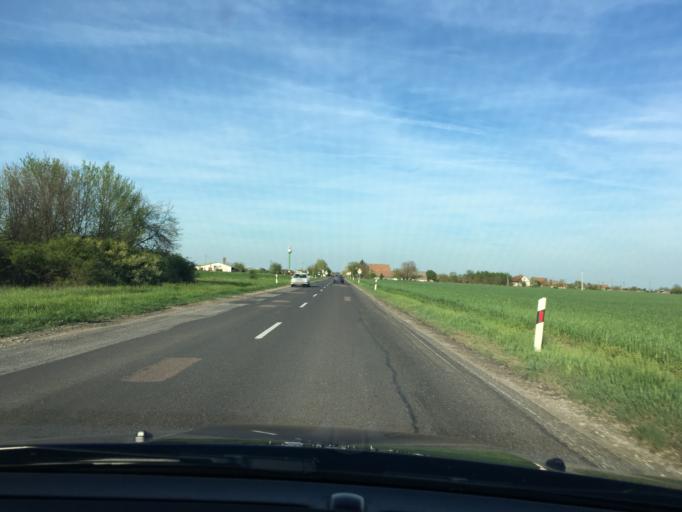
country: HU
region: Hajdu-Bihar
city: Csokmo
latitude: 47.0204
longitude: 21.2716
